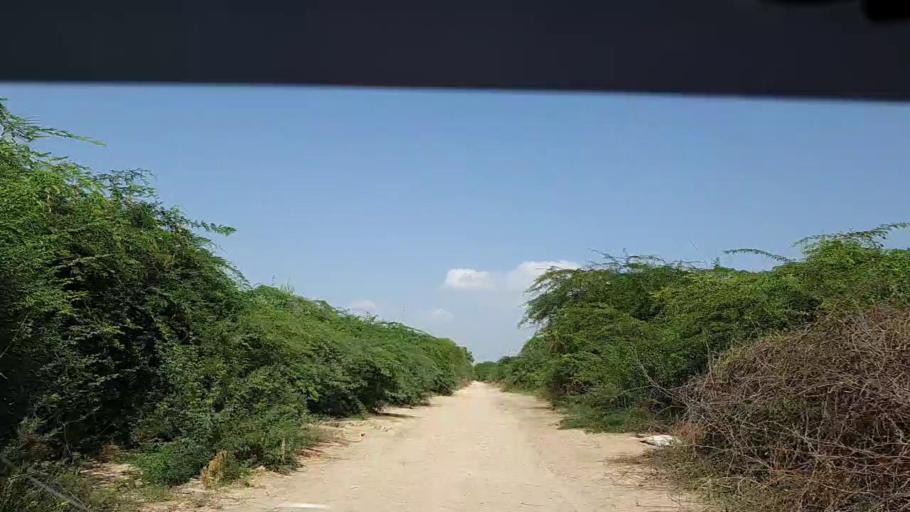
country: PK
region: Sindh
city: Badin
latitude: 24.5873
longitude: 68.7933
